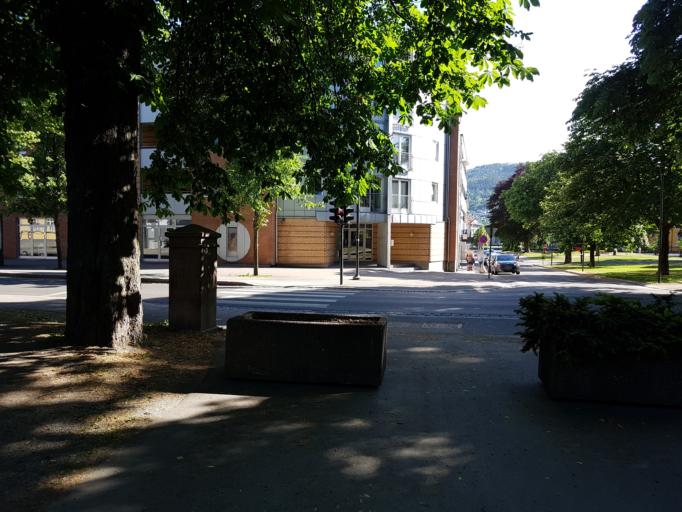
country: NO
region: Buskerud
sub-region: Drammen
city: Drammen
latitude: 59.7457
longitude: 10.2012
